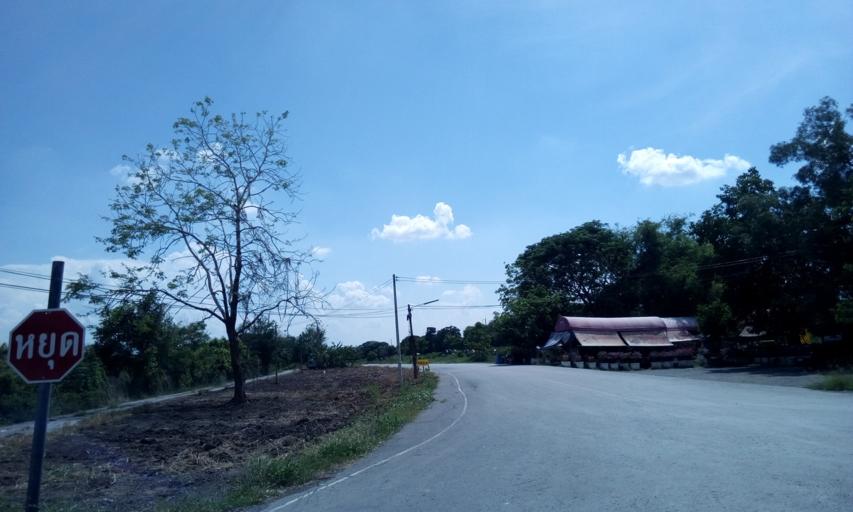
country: TH
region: Nakhon Nayok
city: Ongkharak
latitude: 14.0831
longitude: 100.9140
